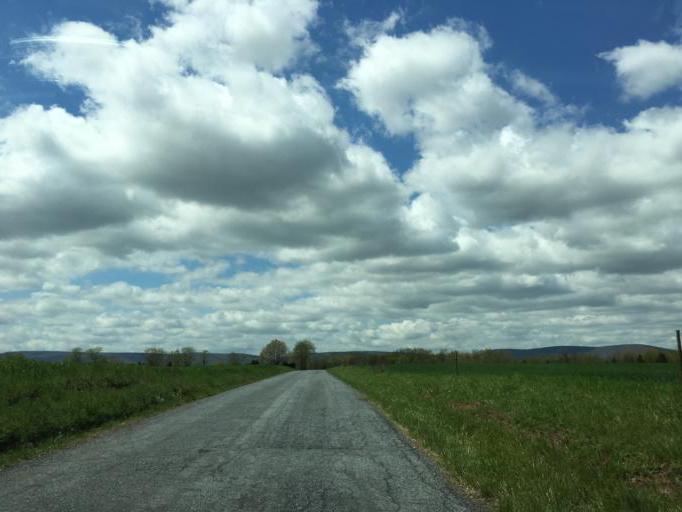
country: US
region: Maryland
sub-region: Frederick County
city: Thurmont
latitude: 39.6025
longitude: -77.3455
